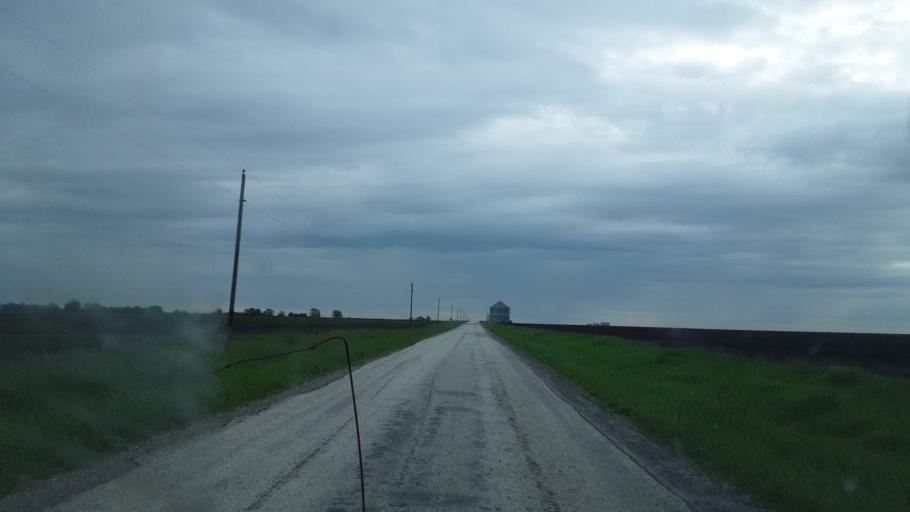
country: US
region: Illinois
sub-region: McDonough County
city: Macomb
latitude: 40.3822
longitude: -90.5800
